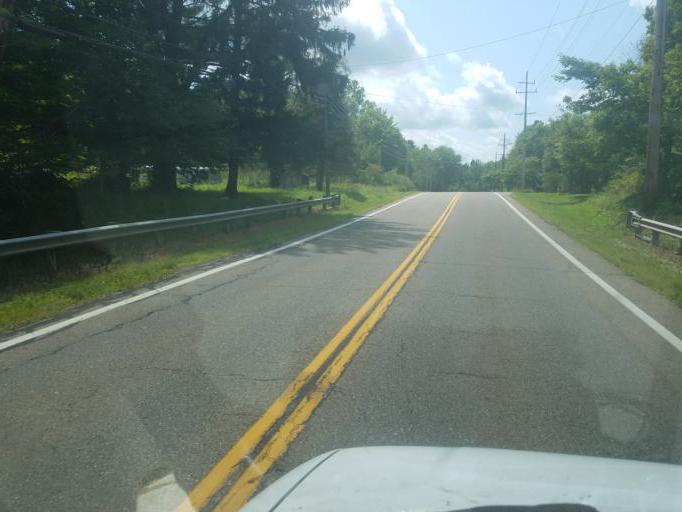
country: US
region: Ohio
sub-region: Ashtabula County
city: Roaming Shores
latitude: 41.6530
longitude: -80.8643
